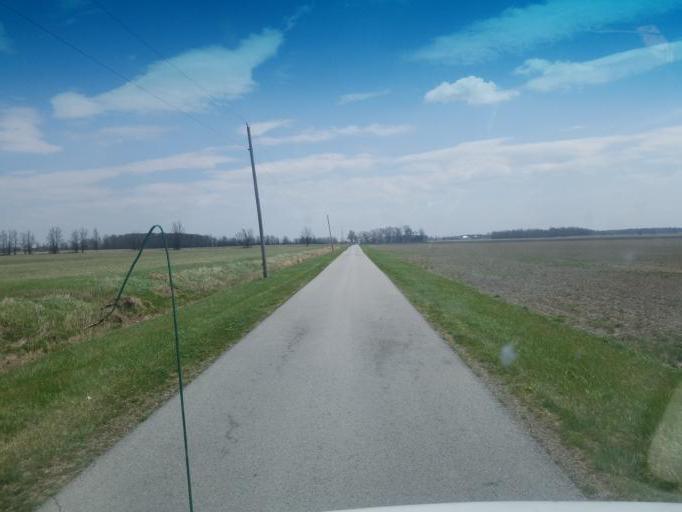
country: US
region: Ohio
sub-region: Hardin County
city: Forest
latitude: 40.7744
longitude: -83.4955
